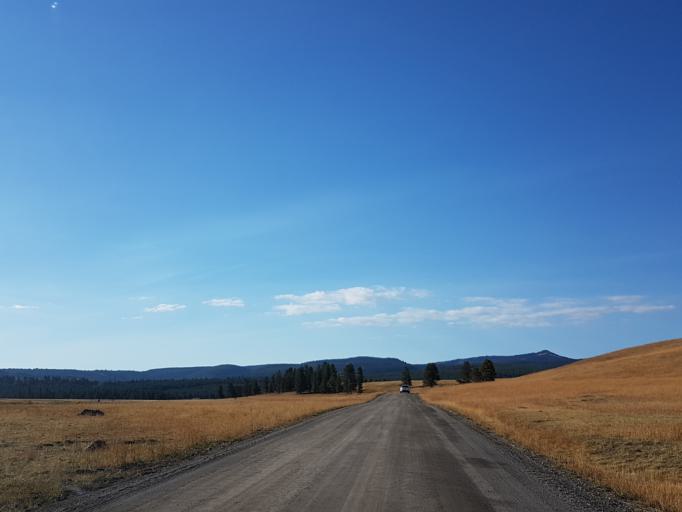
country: US
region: Montana
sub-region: Gallatin County
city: West Yellowstone
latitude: 44.6957
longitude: -111.2137
